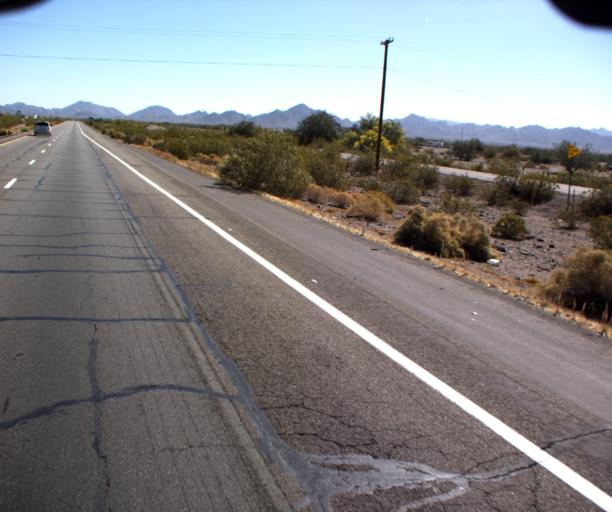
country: US
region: Arizona
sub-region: La Paz County
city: Quartzsite
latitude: 33.6663
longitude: -114.1912
